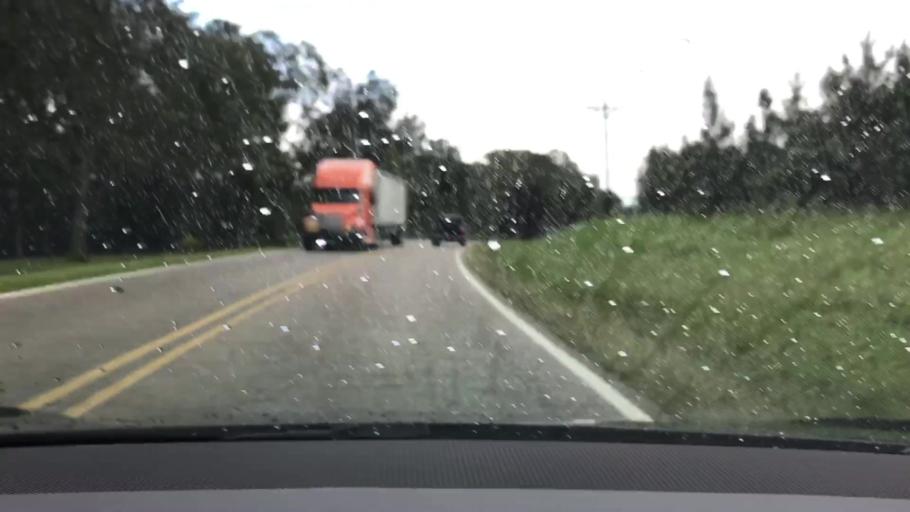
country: US
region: Alabama
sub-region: Geneva County
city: Samson
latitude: 31.1264
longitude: -86.1271
